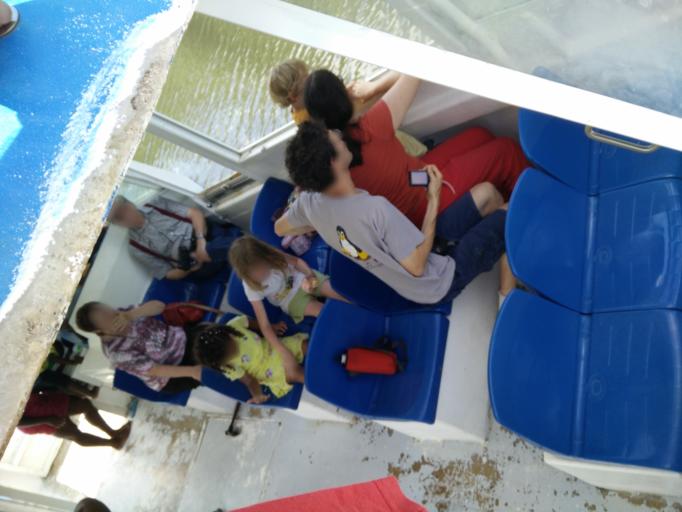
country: GP
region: Guadeloupe
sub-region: Guadeloupe
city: Petit-Canal
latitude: 16.3536
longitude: -61.4925
